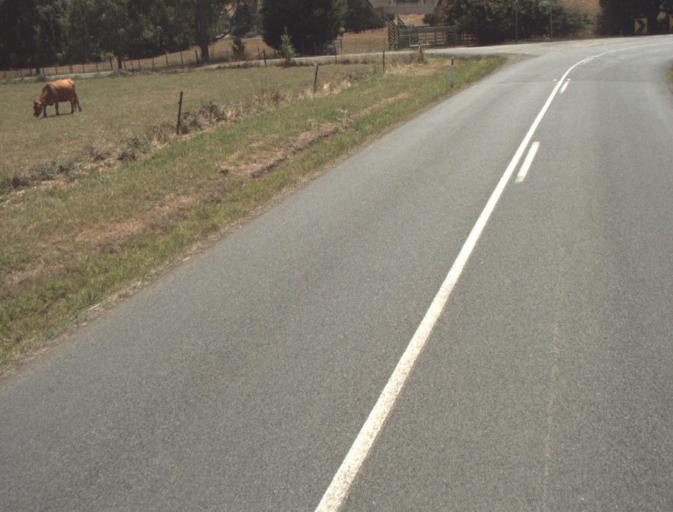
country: AU
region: Tasmania
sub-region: Launceston
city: Mayfield
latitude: -41.2595
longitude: 147.1360
